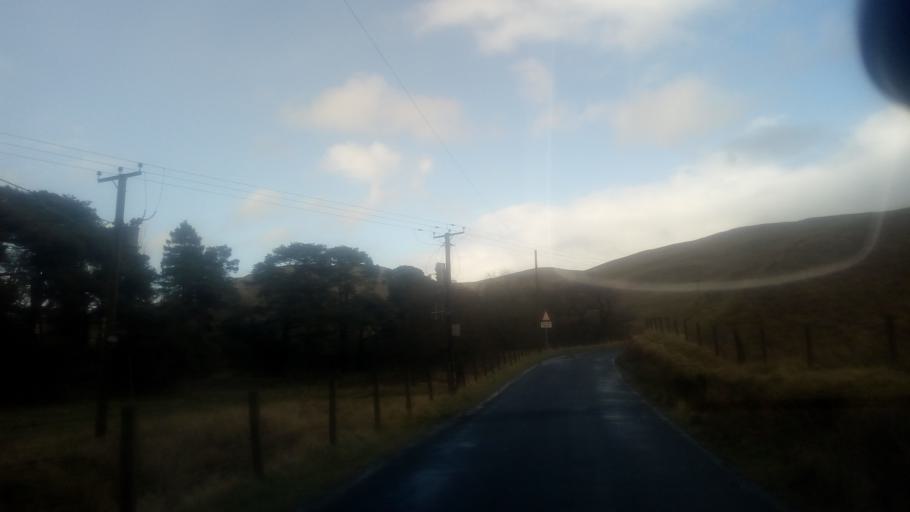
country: GB
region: Scotland
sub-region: The Scottish Borders
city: Innerleithen
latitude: 55.4555
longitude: -3.1011
